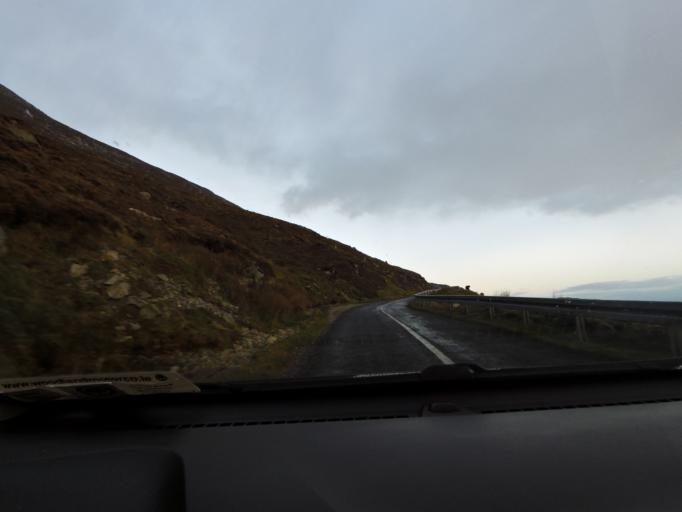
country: IE
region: Connaught
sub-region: Maigh Eo
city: Belmullet
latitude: 53.9710
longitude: -10.1876
